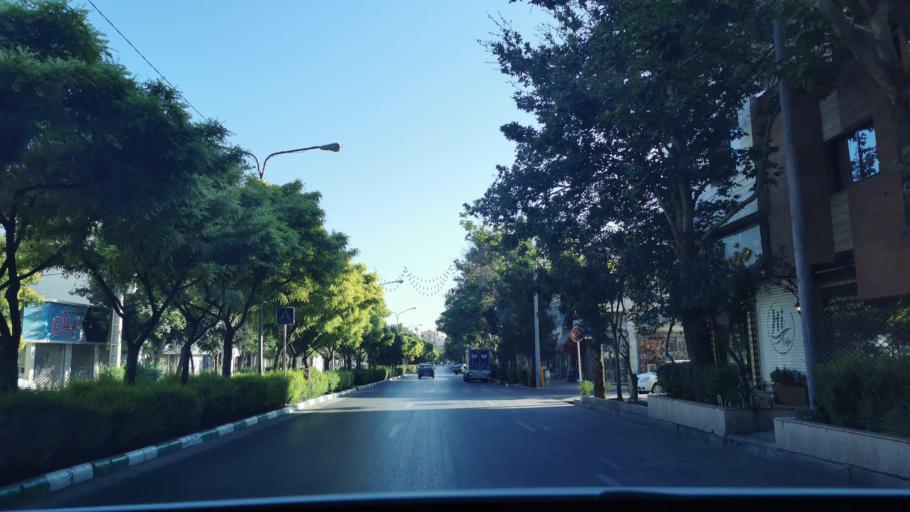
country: IR
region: Razavi Khorasan
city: Mashhad
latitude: 36.2941
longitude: 59.5681
